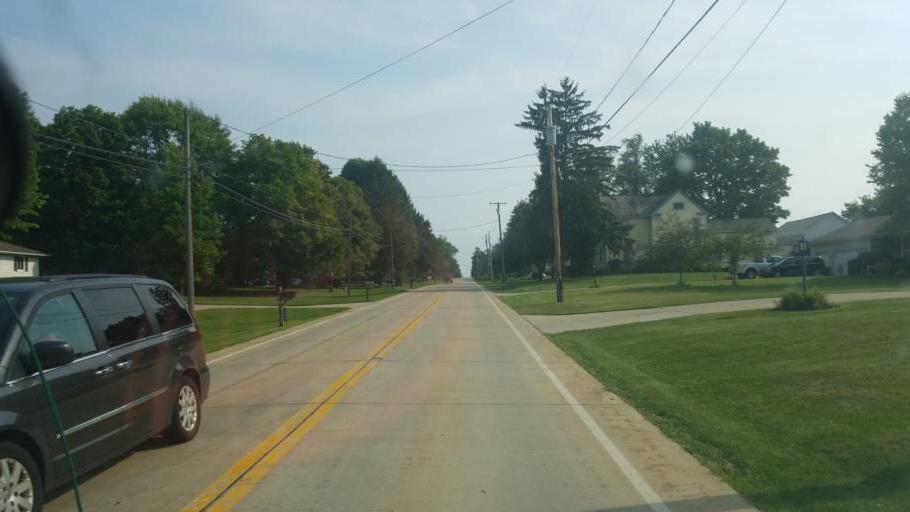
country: US
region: Ohio
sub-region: Medina County
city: Medina
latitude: 41.1156
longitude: -81.8840
